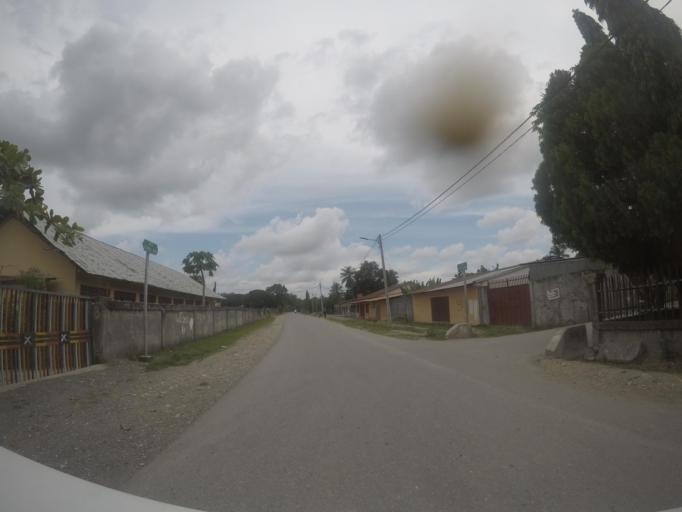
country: TL
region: Viqueque
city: Viqueque
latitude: -8.8690
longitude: 126.3646
